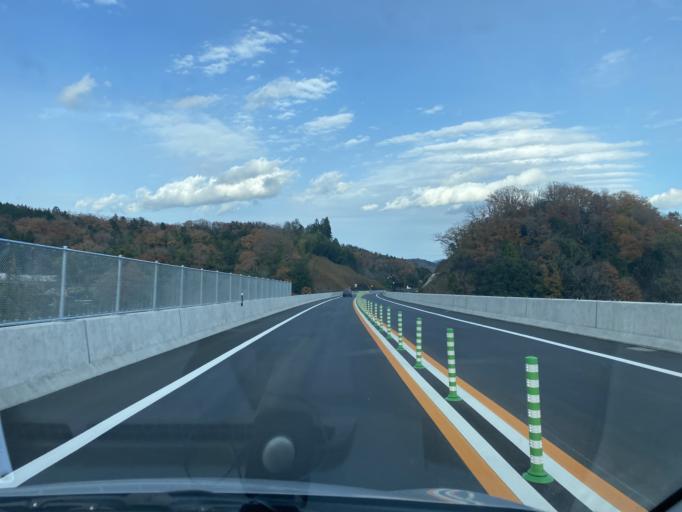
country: JP
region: Hyogo
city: Toyooka
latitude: 35.4840
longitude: 134.7704
